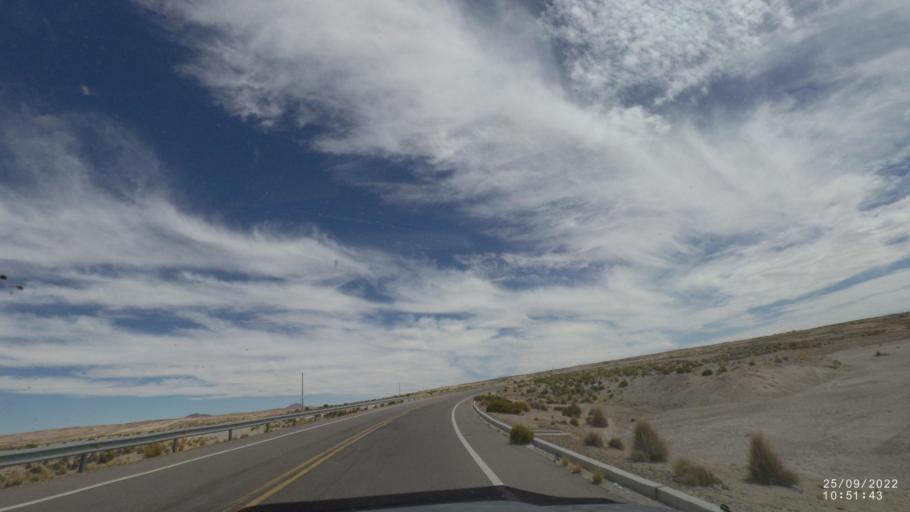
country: BO
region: Oruro
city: Challapata
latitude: -19.5588
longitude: -66.8520
